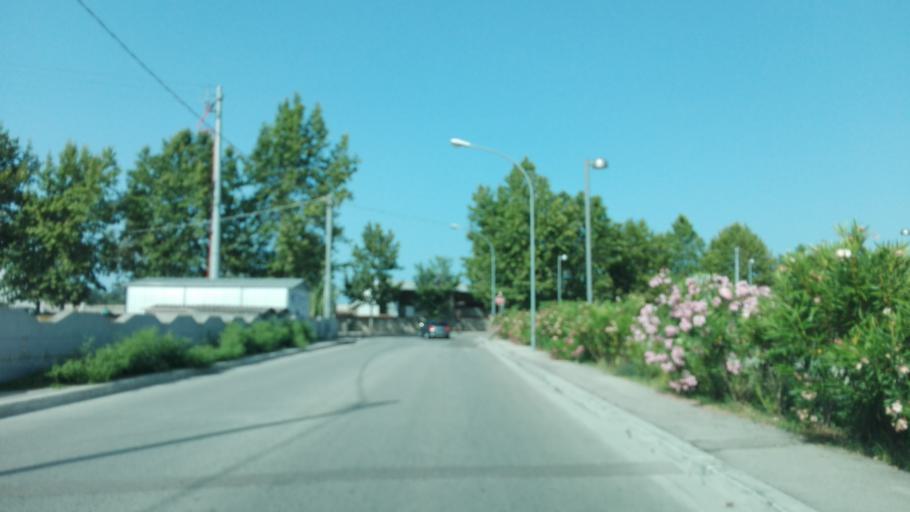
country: IT
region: Abruzzo
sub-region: Provincia di Pescara
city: Montesilvano Marina
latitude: 42.5129
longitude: 14.1385
